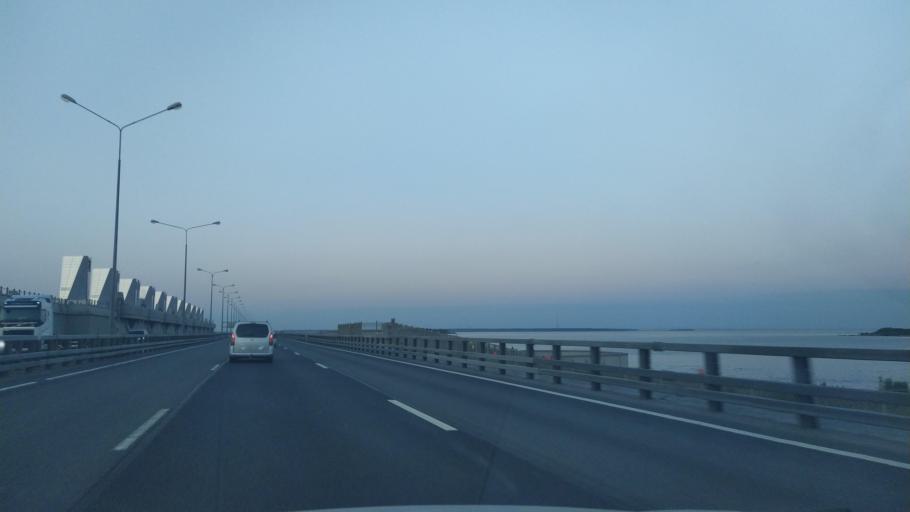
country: RU
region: St.-Petersburg
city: Kronshtadt
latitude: 60.0278
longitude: 29.8600
